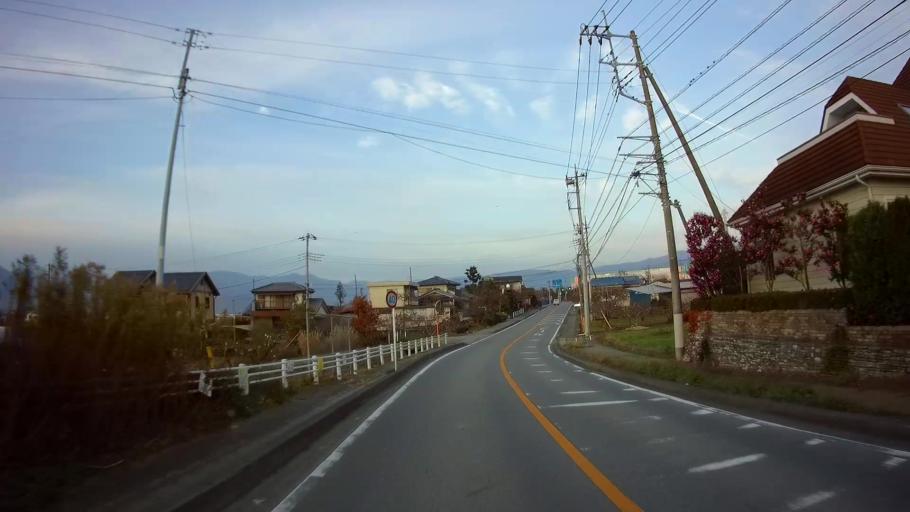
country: JP
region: Yamanashi
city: Isawa
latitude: 35.6269
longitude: 138.6778
